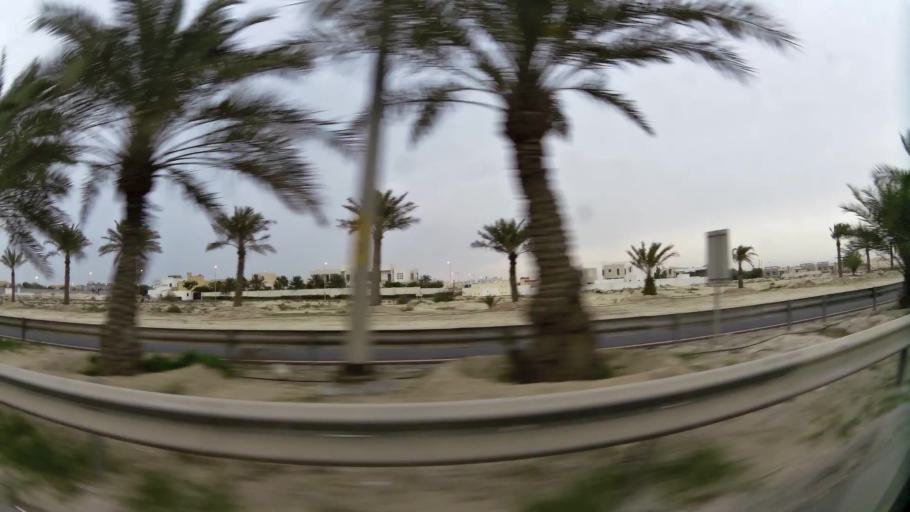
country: BH
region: Northern
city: Ar Rifa'
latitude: 26.1466
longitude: 50.5396
